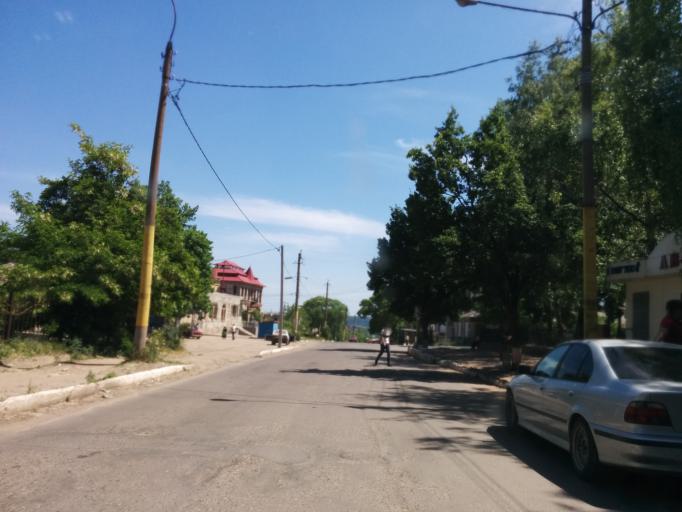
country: MD
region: Raionul Soroca
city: Soroca
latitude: 48.1614
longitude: 28.2911
